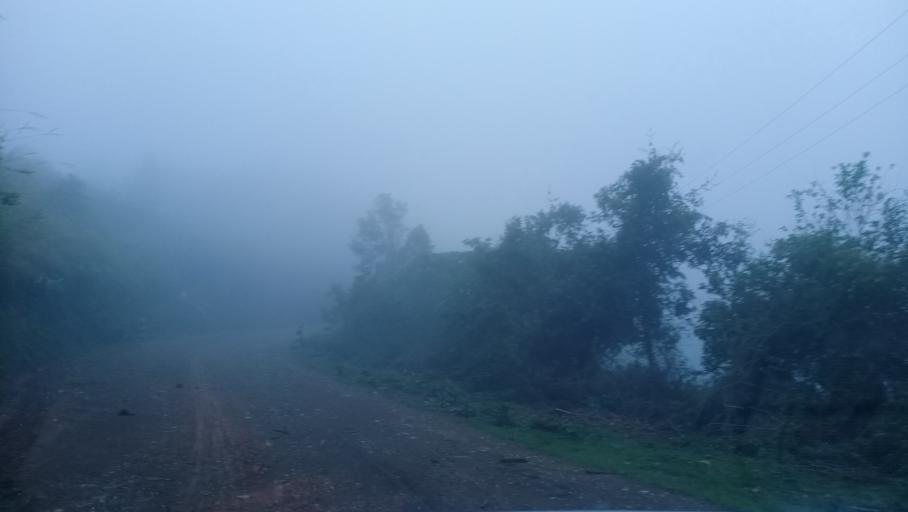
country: LA
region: Phongsali
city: Phongsali
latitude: 21.5191
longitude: 102.2027
